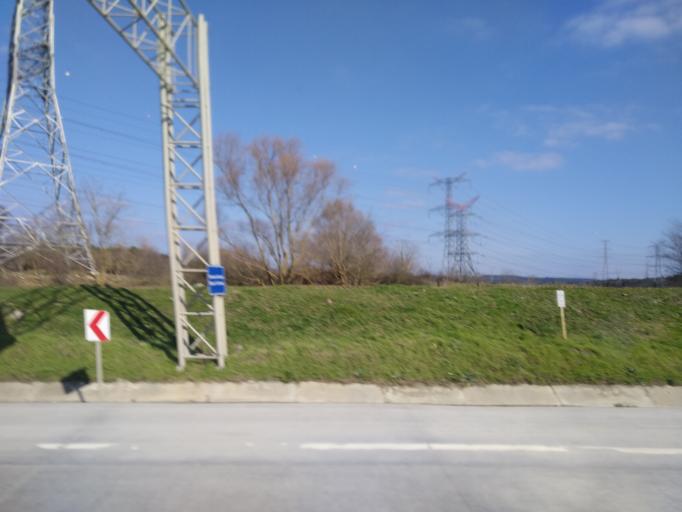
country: TR
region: Istanbul
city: Kemerburgaz
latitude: 41.1309
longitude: 28.9437
